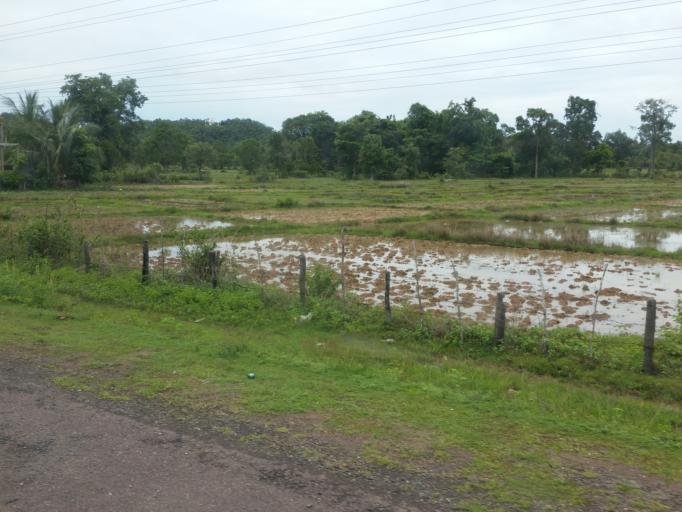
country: LA
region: Champasak
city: Khong
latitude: 14.1175
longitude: 105.8735
